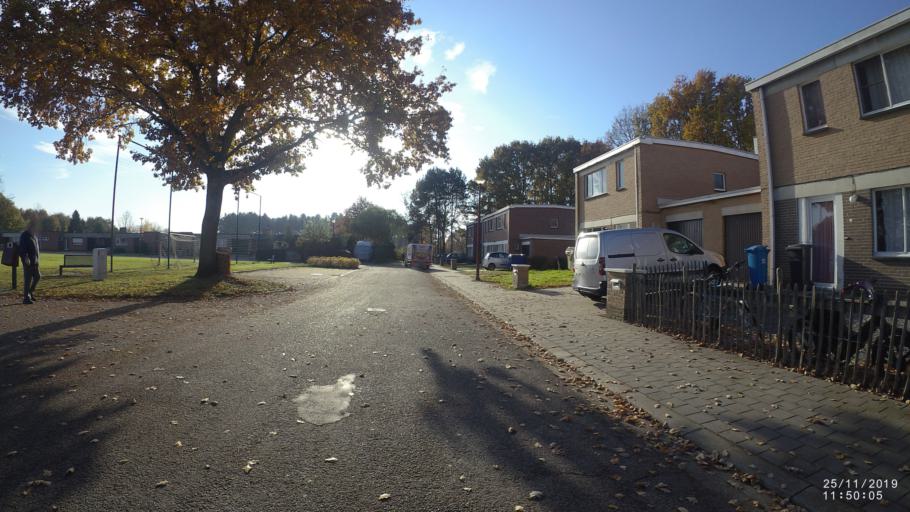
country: BE
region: Flanders
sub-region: Provincie Vlaams-Brabant
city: Aarschot
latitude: 51.0031
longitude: 4.8452
